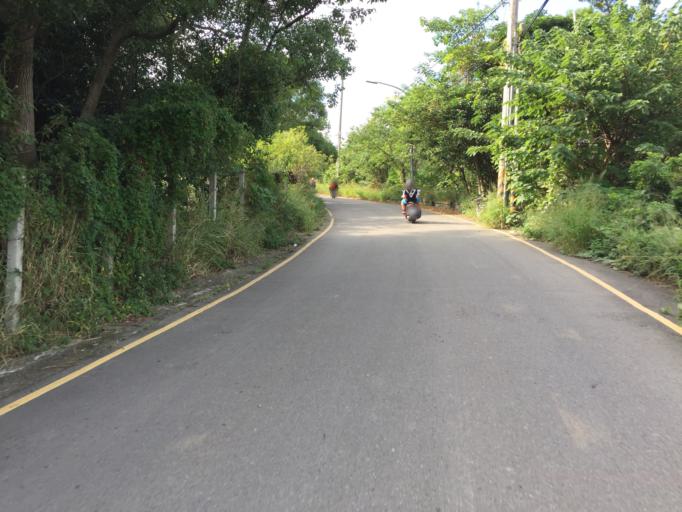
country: TW
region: Taiwan
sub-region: Hsinchu
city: Hsinchu
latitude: 24.7772
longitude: 120.9302
